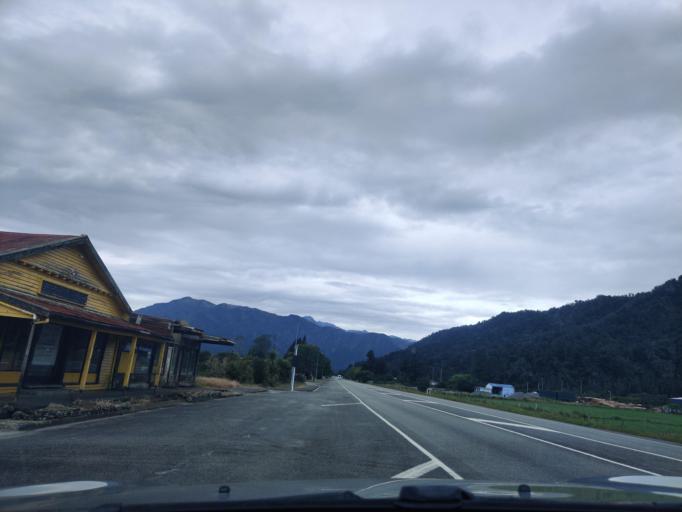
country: NZ
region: West Coast
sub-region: Westland District
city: Hokitika
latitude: -43.1484
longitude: 170.5523
